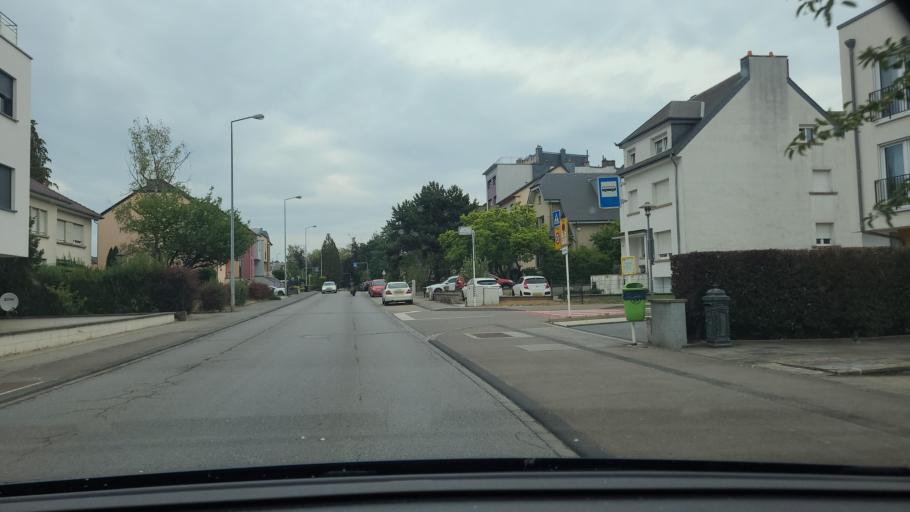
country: LU
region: Luxembourg
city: Belvaux
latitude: 49.5211
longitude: 5.9130
